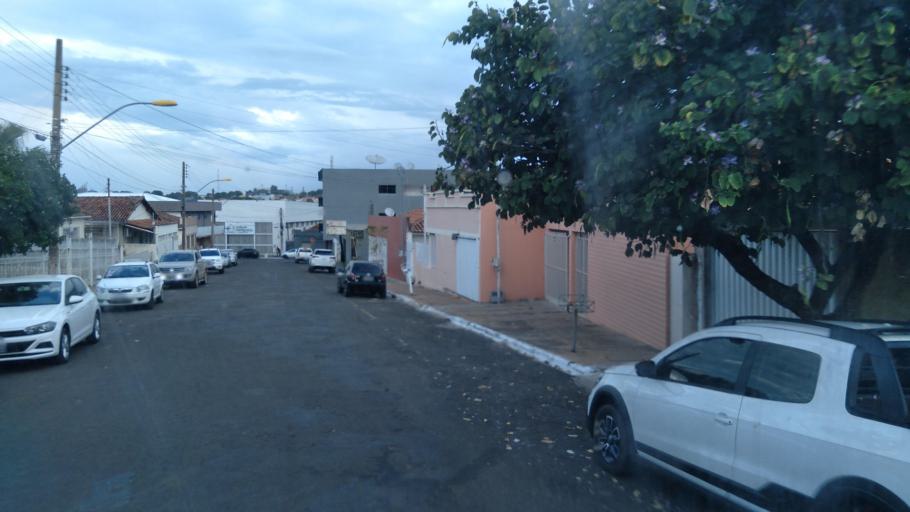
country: BR
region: Goias
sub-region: Mineiros
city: Mineiros
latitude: -17.5698
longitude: -52.5556
